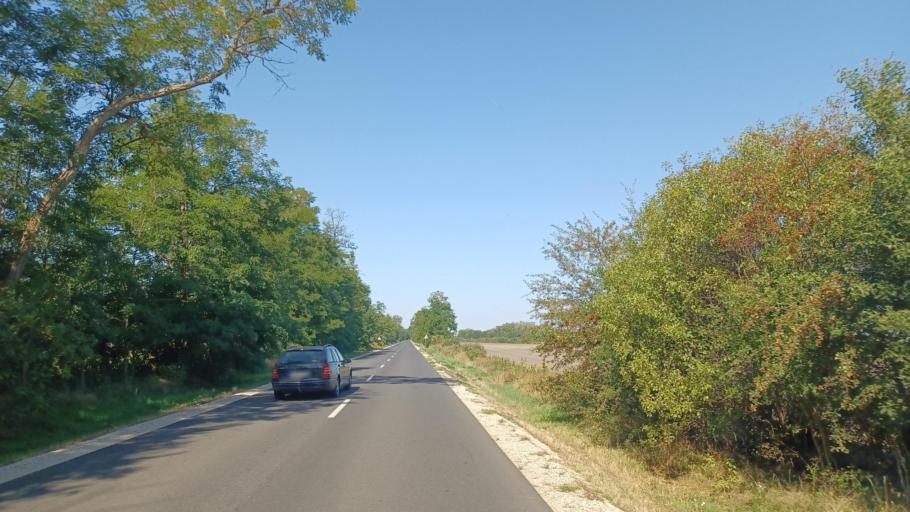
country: HU
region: Tolna
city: Nemetker
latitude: 46.7353
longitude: 18.7176
